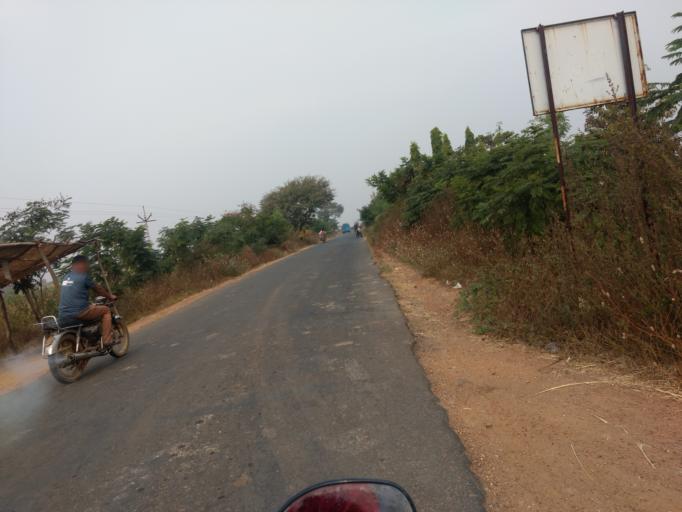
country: IN
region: Maharashtra
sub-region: Chandrapur
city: Mul
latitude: 19.9171
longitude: 79.9182
